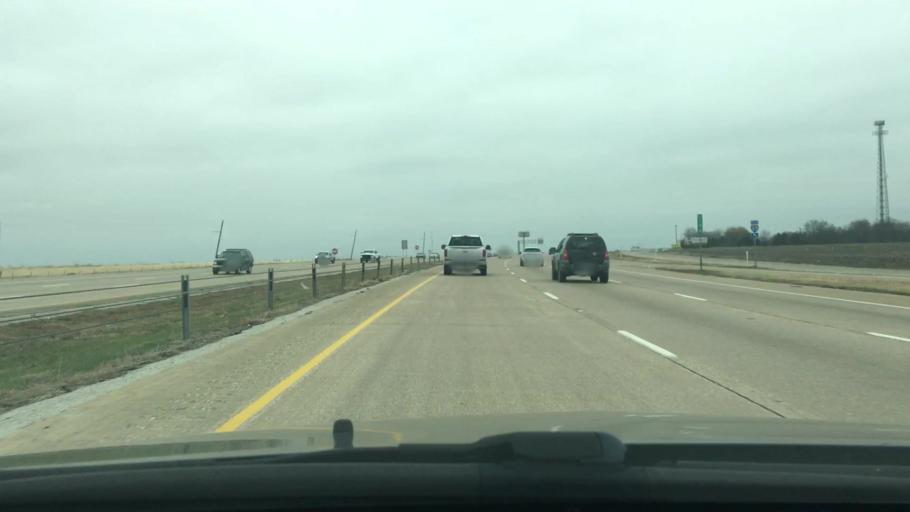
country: US
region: Texas
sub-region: Ellis County
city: Ennis
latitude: 32.2694
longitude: -96.5108
